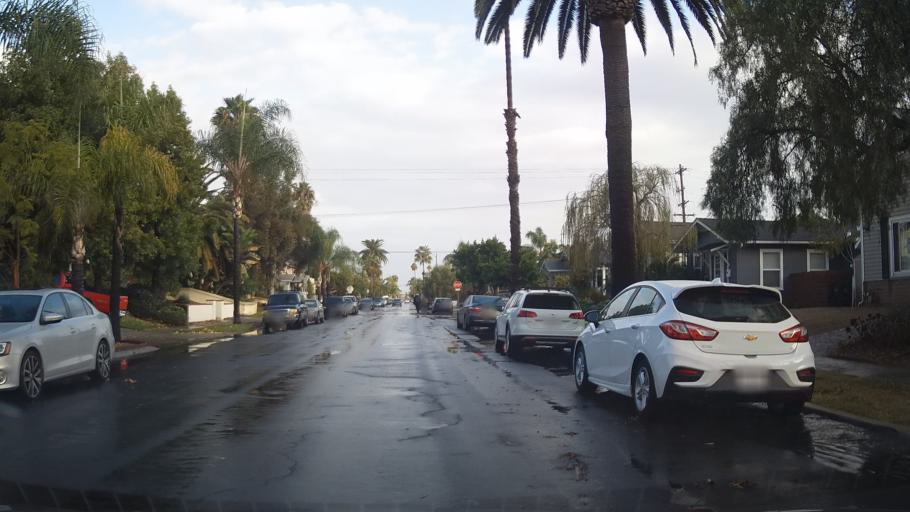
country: US
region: California
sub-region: San Diego County
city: San Diego
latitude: 32.7583
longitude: -117.1240
